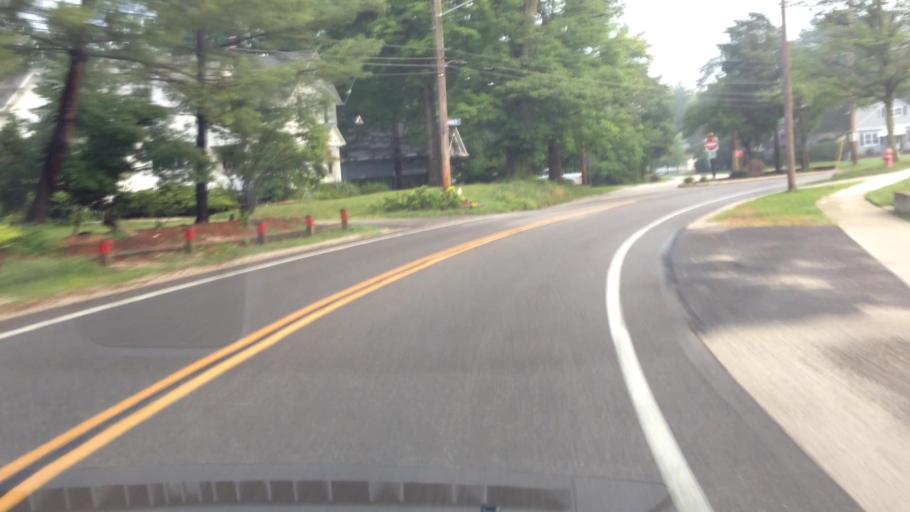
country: US
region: Ohio
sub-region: Cuyahoga County
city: Berea
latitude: 41.3609
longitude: -81.8441
